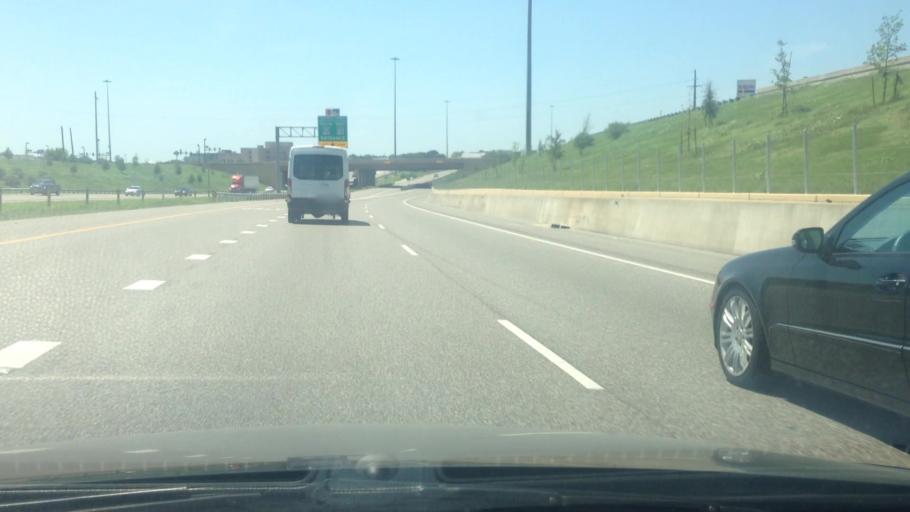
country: US
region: Texas
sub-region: Tarrant County
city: Bedford
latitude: 32.8421
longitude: -97.1180
